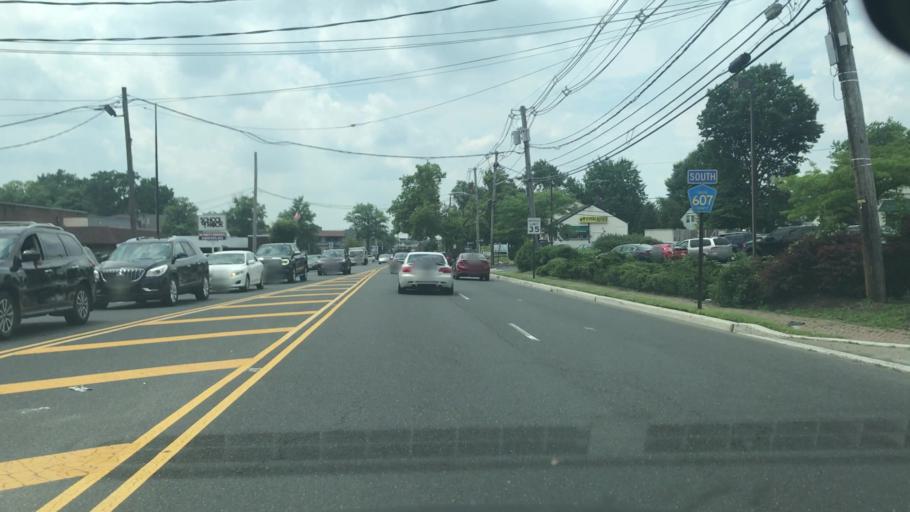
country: US
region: New Jersey
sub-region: Union County
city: Clark
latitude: 40.6300
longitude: -74.3105
